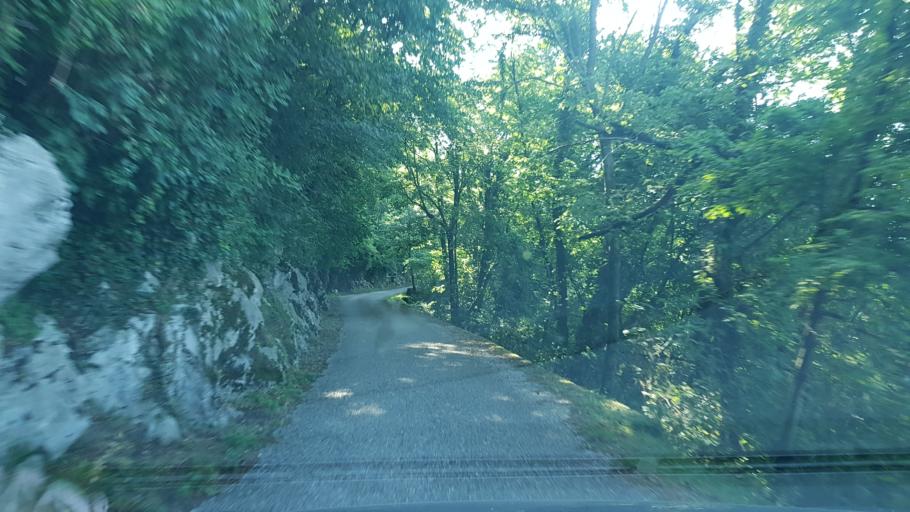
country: IT
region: Friuli Venezia Giulia
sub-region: Provincia di Udine
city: Nimis
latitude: 46.2353
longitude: 13.2462
